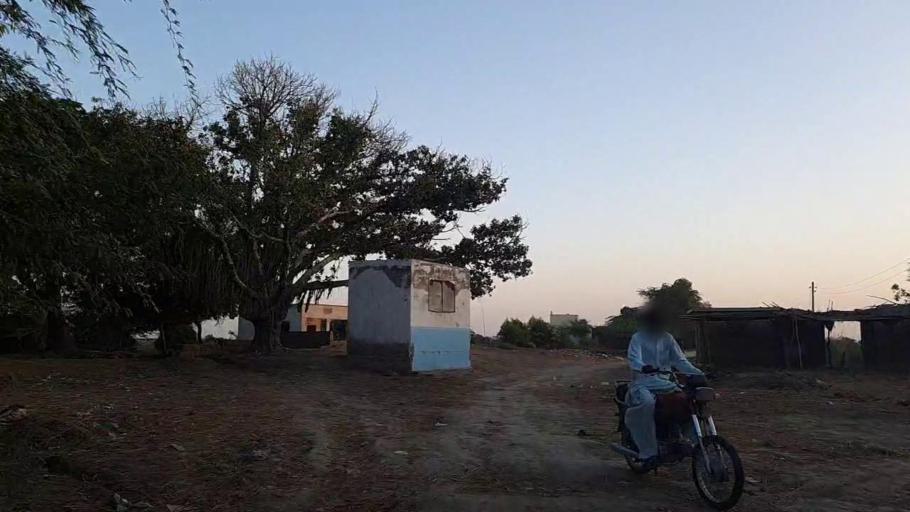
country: PK
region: Sindh
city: Mirpur Batoro
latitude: 24.6440
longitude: 68.1899
